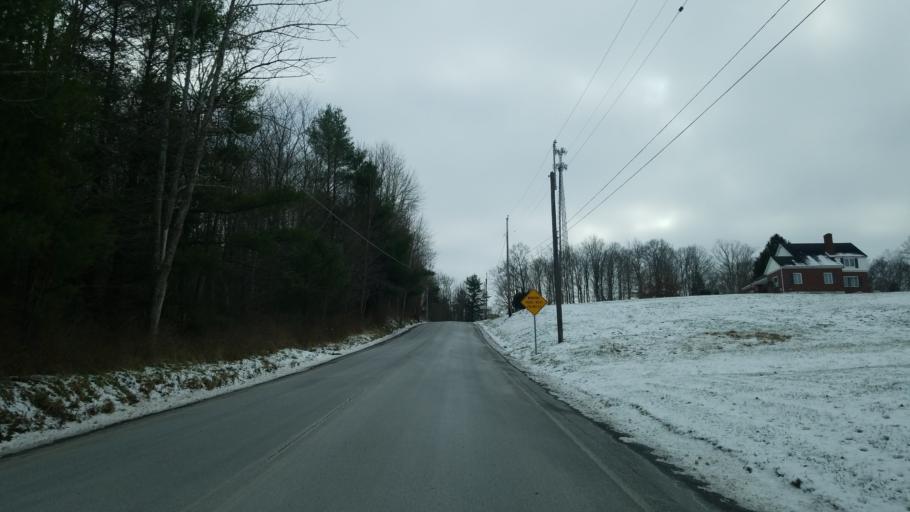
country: US
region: Pennsylvania
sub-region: Clearfield County
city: Sandy
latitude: 41.1056
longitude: -78.7599
